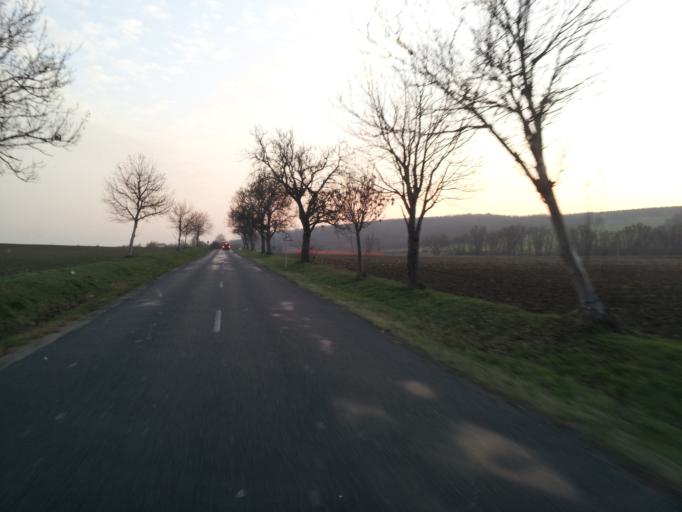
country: HU
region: Zala
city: Cserszegtomaj
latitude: 46.8339
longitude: 17.1956
